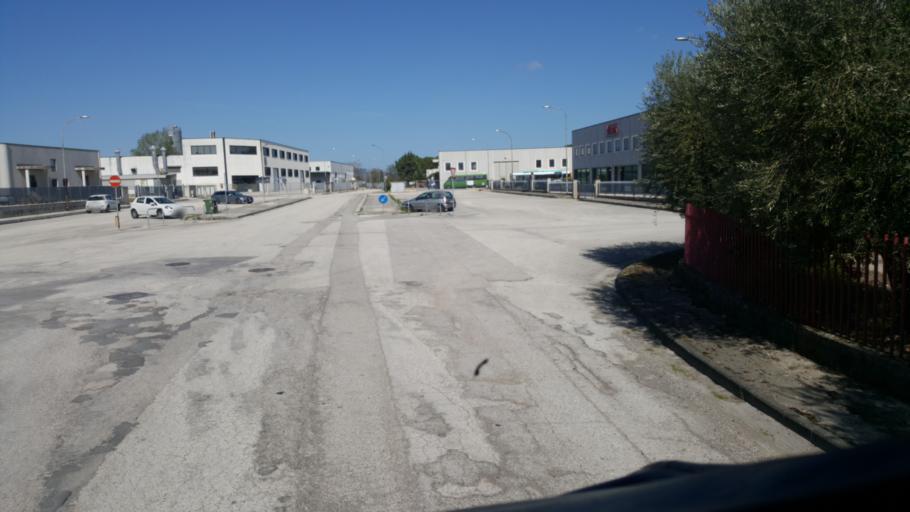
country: IT
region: The Marches
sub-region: Provincia di Macerata
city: Montecassiano
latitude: 43.3550
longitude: 13.4599
